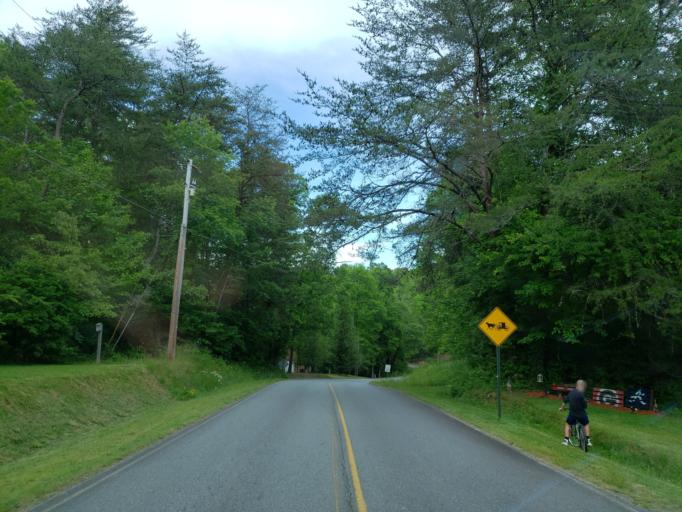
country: US
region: Georgia
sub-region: Fannin County
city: Blue Ridge
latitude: 34.8677
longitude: -84.3683
